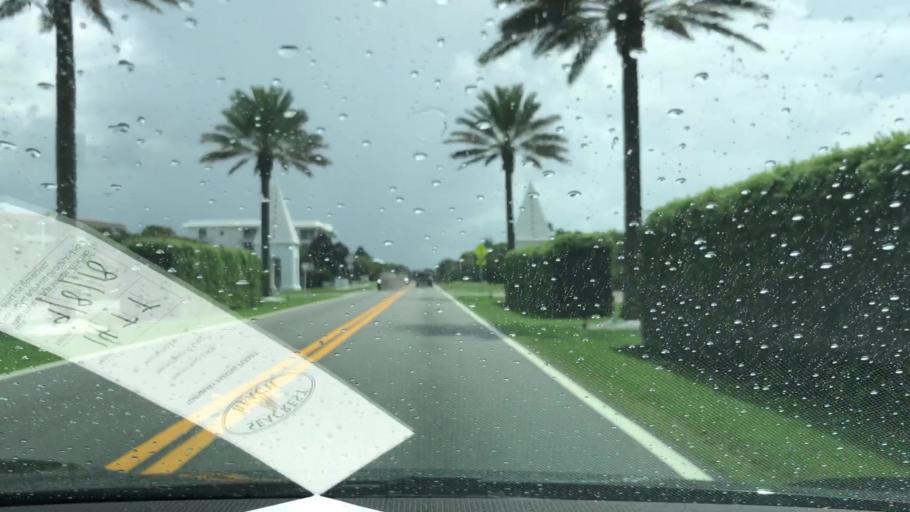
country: US
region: Florida
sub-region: Bay County
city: Laguna Beach
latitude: 30.2838
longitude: -86.0264
